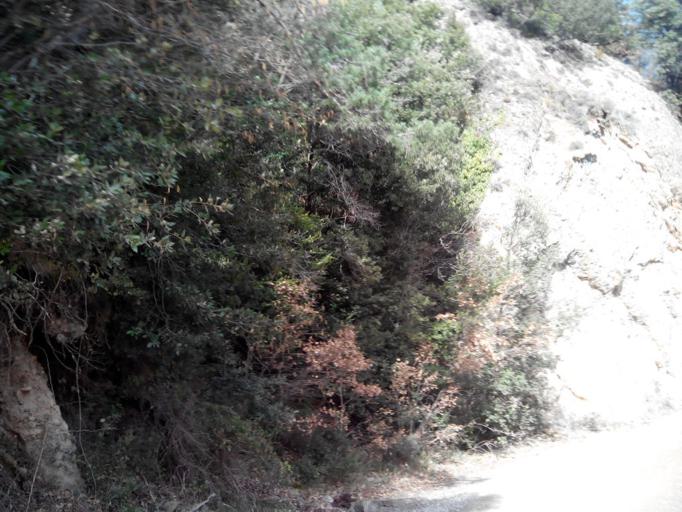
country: ES
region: Catalonia
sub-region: Provincia de Barcelona
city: Vilada
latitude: 42.1717
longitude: 1.9292
